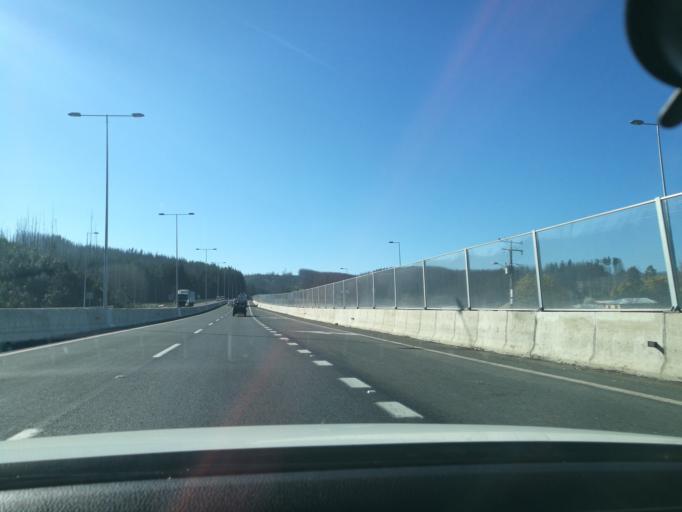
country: CL
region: Biobio
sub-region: Provincia de Concepcion
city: Penco
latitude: -36.8561
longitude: -72.8746
